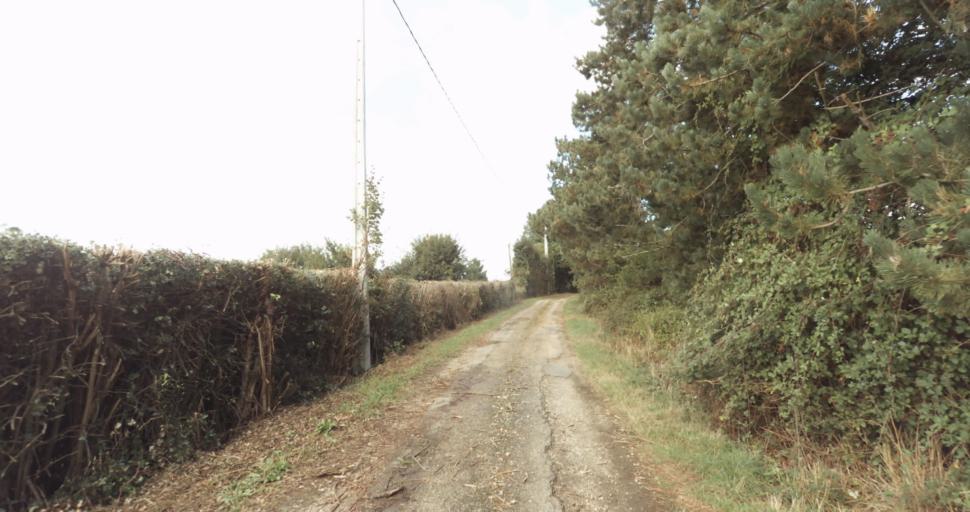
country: FR
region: Lower Normandy
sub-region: Departement du Calvados
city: Orbec
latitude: 48.9264
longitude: 0.3708
